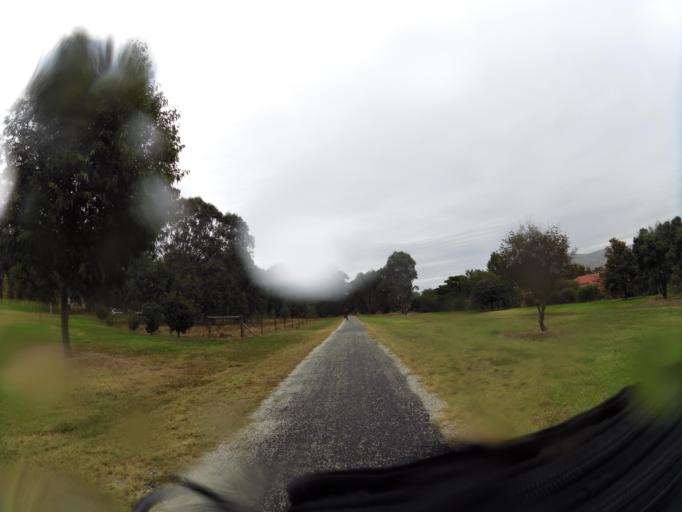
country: AU
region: New South Wales
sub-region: Albury Municipality
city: East Albury
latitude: -36.2168
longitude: 147.1910
